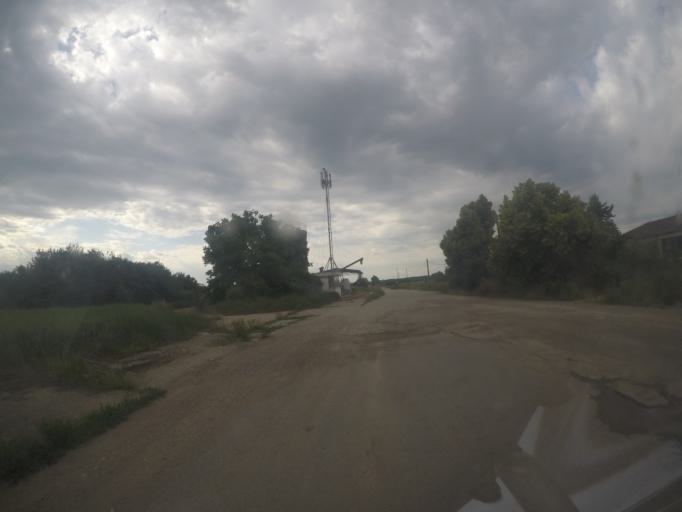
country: RS
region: Central Serbia
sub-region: Belgrade
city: Zemun
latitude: 44.8869
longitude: 20.3828
